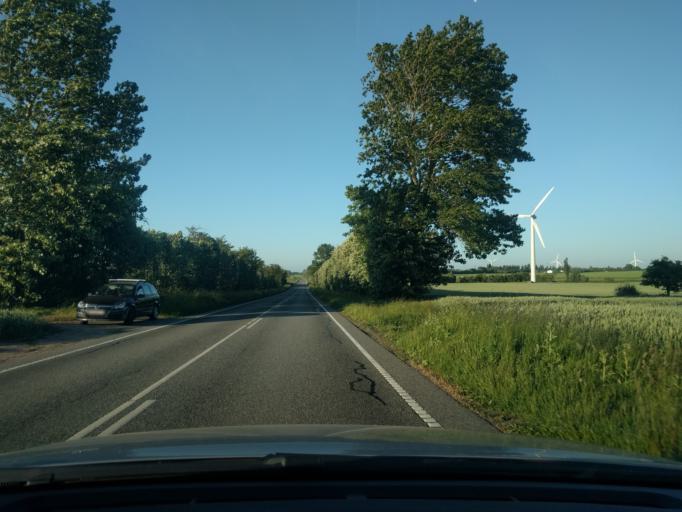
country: DK
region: South Denmark
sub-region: Kerteminde Kommune
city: Kerteminde
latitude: 55.4843
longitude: 10.6222
